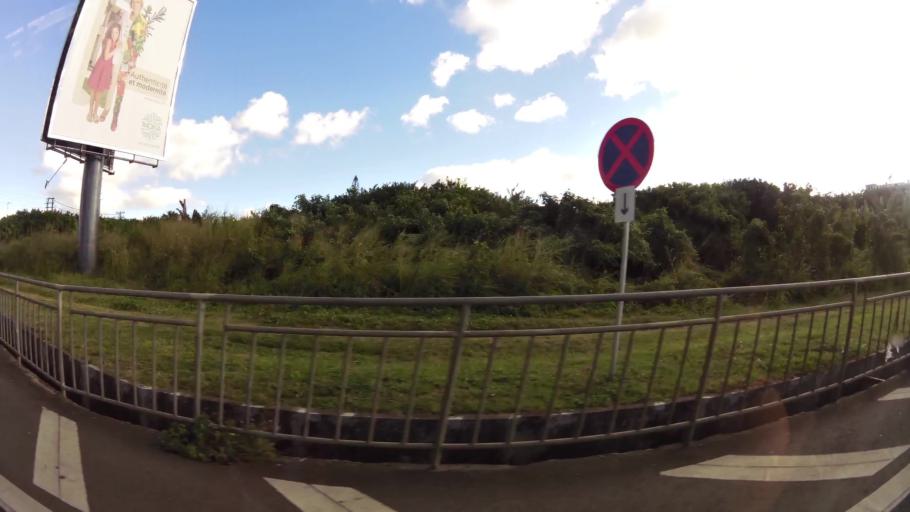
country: MU
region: Plaines Wilhems
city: Quatre Bornes
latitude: -20.2621
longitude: 57.4906
